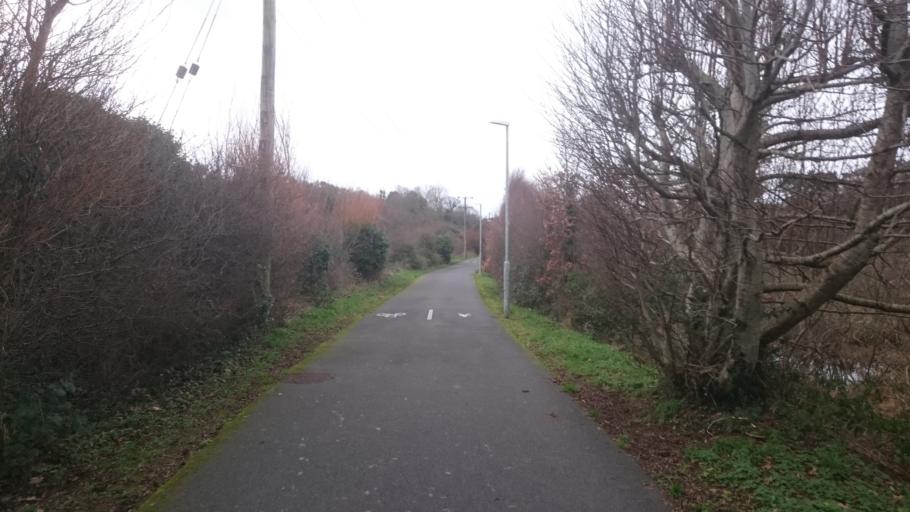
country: IE
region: Connaught
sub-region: Maigh Eo
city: Westport
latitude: 53.7949
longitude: -9.5427
